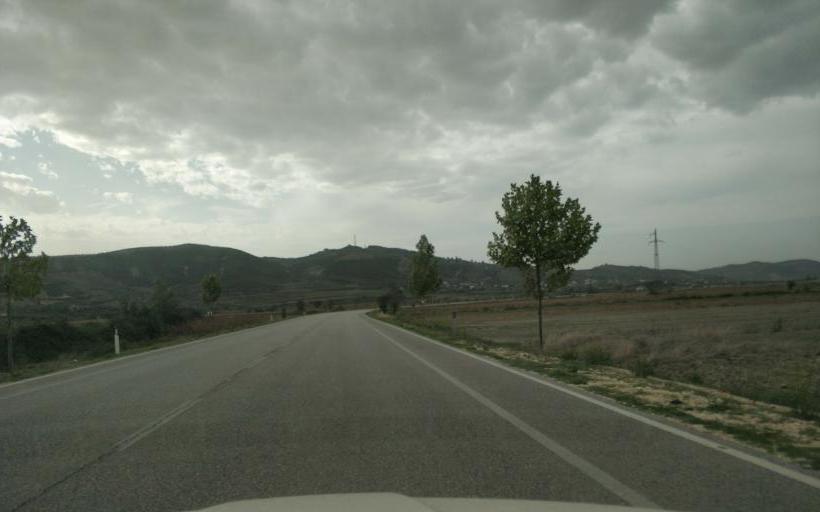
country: AL
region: Fier
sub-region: Rrethi i Fierit
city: Cakran
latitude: 40.5703
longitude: 19.6309
